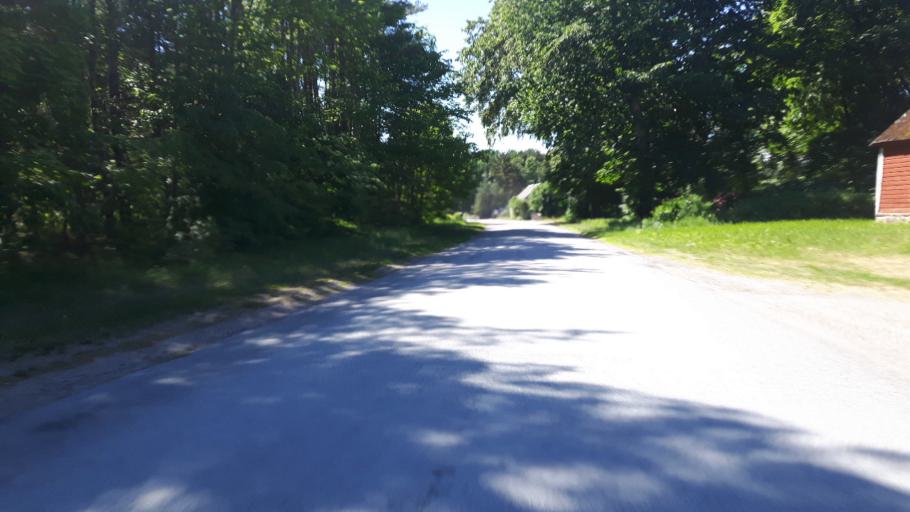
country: LV
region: Salacgrivas
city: Ainazi
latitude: 58.0363
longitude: 24.4628
